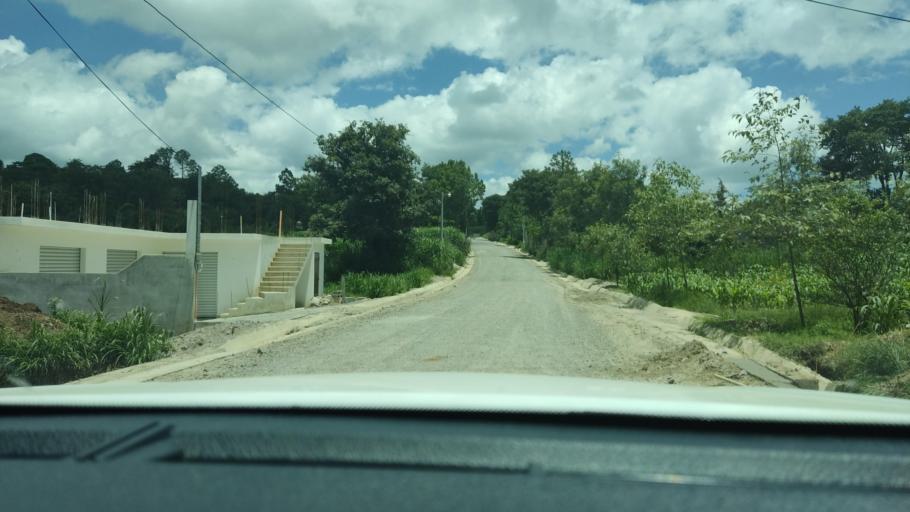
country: GT
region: Chimaltenango
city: San Martin Jilotepeque
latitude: 14.7985
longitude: -90.8160
